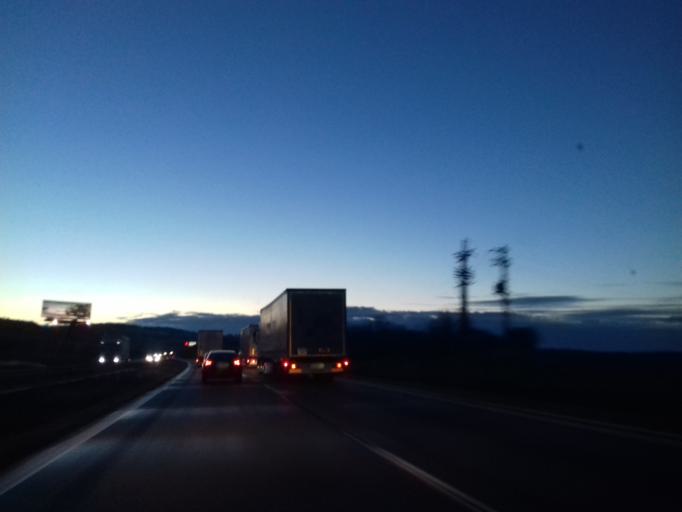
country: CZ
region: Vysocina
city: Krizanov
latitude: 49.3201
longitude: 16.0881
